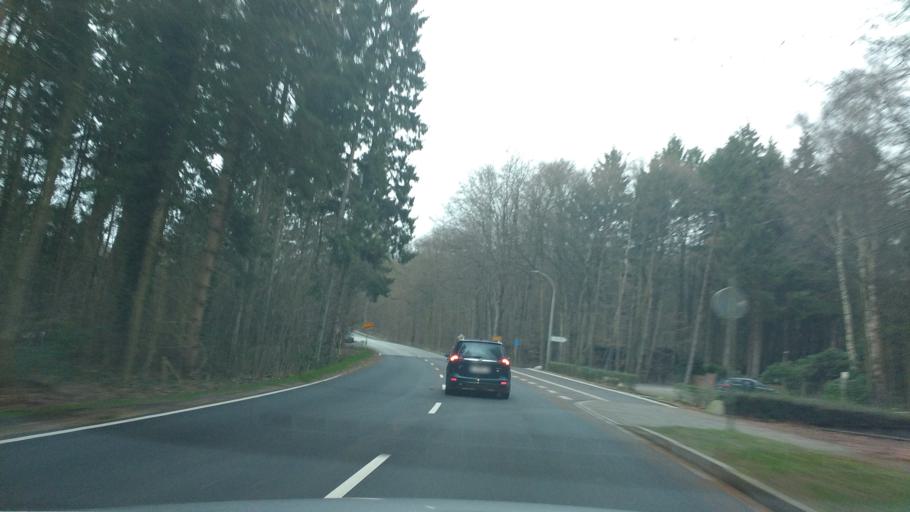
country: DE
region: Schleswig-Holstein
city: Itzehoe
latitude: 53.9342
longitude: 9.5386
